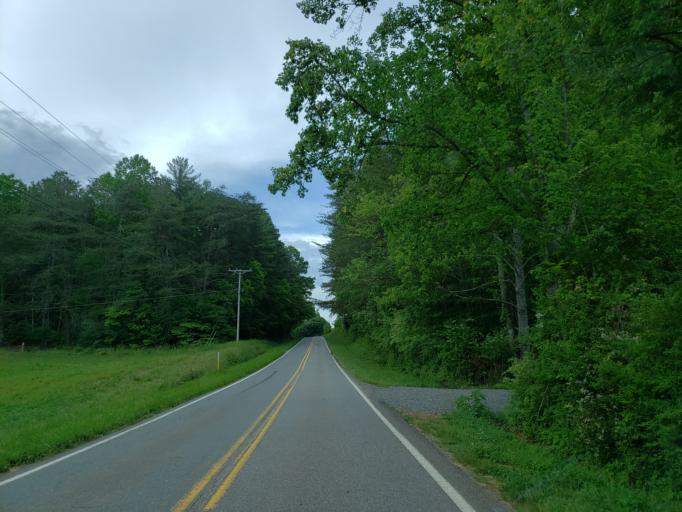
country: US
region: Georgia
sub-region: Fannin County
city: Blue Ridge
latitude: 34.8631
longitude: -84.3710
